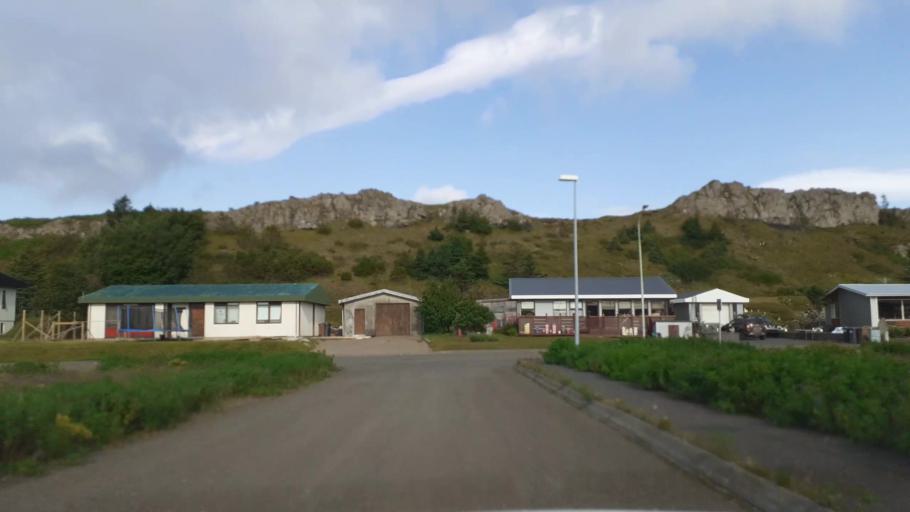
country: IS
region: East
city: Reydarfjoerdur
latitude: 64.6537
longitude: -14.2813
